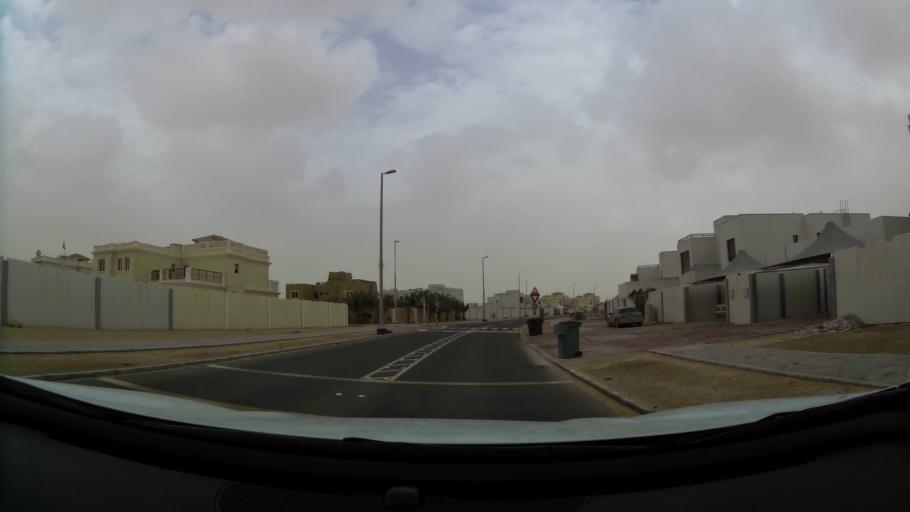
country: AE
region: Abu Dhabi
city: Abu Dhabi
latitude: 24.4440
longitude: 54.7166
